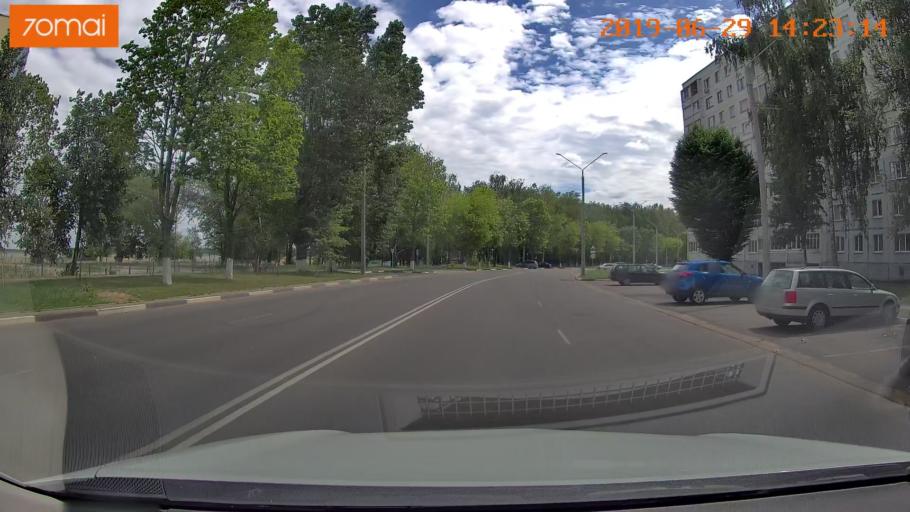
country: BY
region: Minsk
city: Salihorsk
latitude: 52.7871
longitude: 27.5541
